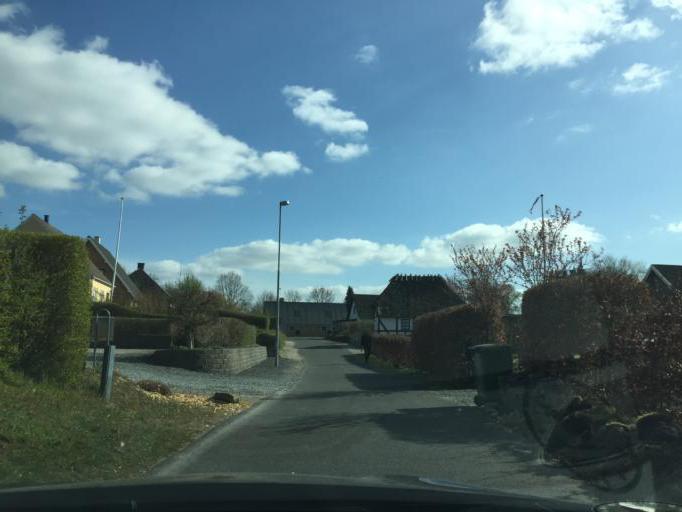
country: DK
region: South Denmark
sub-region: Faaborg-Midtfyn Kommune
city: Arslev
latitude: 55.3102
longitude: 10.4930
